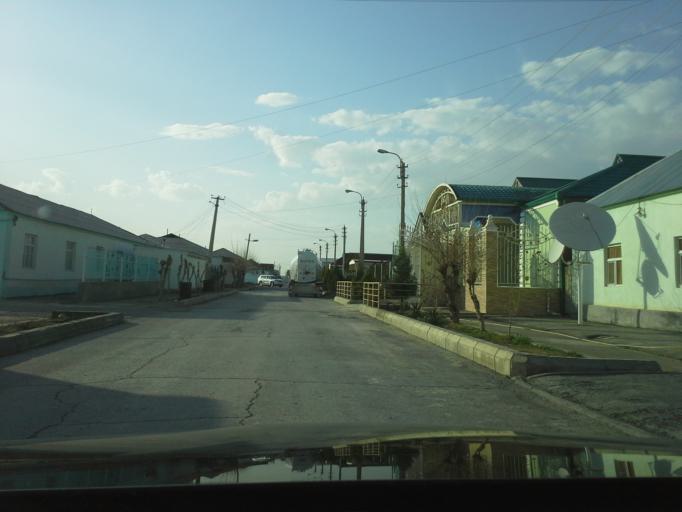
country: TM
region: Ahal
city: Abadan
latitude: 38.0203
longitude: 58.2294
